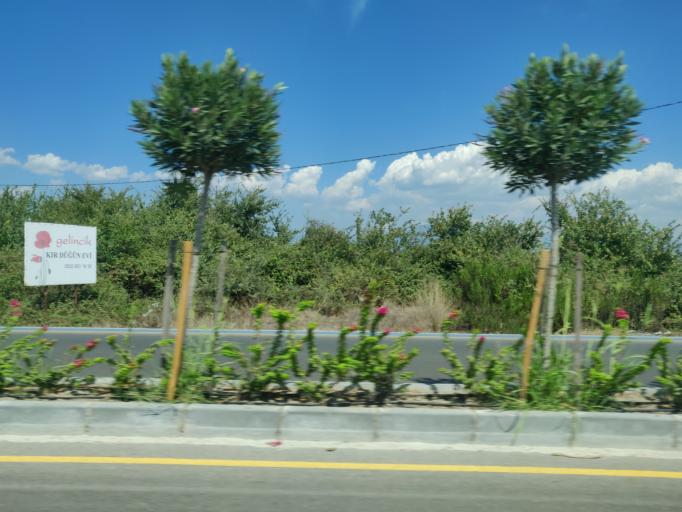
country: TR
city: Dalyan
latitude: 36.8401
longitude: 28.6562
